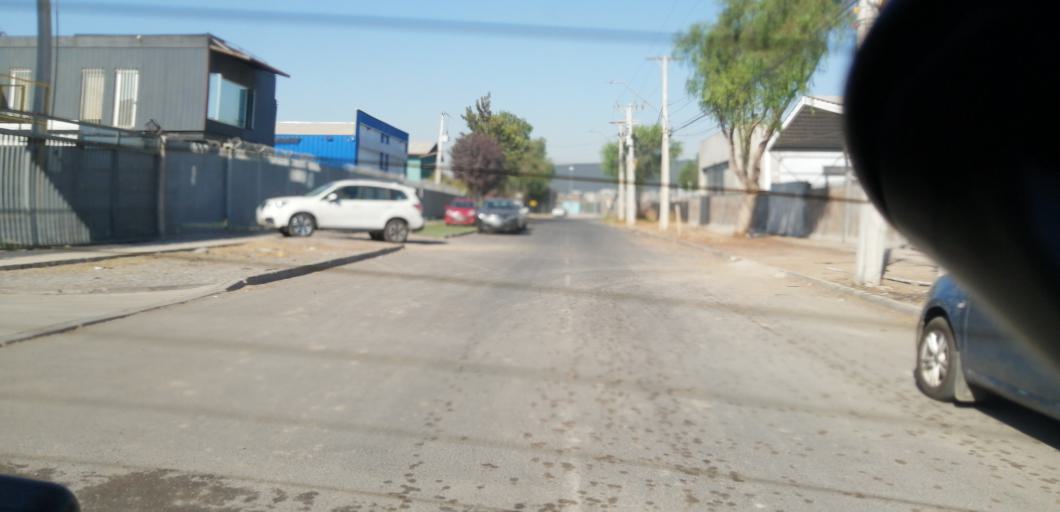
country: CL
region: Santiago Metropolitan
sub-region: Provincia de Santiago
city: Lo Prado
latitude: -33.3840
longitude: -70.7773
